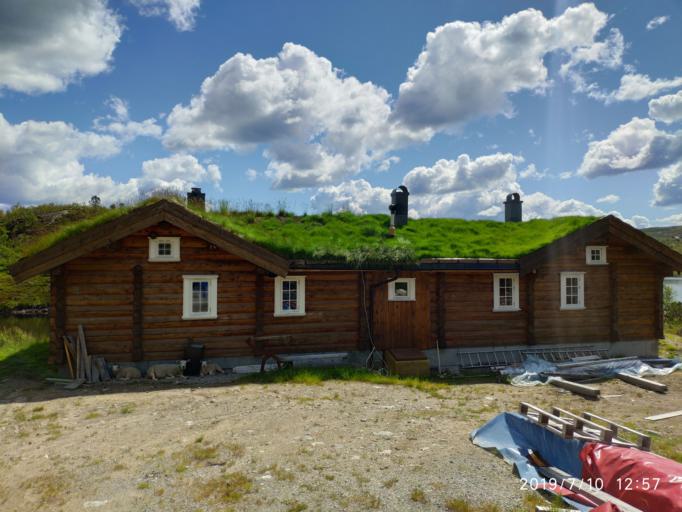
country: NO
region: Aust-Agder
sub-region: Valle
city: Valle
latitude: 59.0595
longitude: 7.3734
